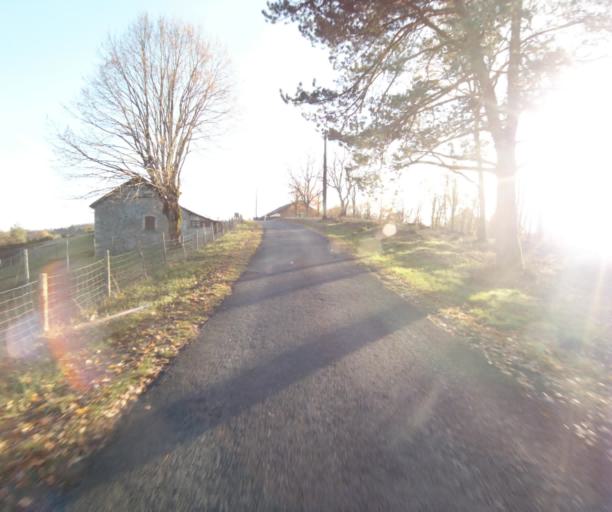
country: FR
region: Limousin
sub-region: Departement de la Correze
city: Laguenne
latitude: 45.2305
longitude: 1.8009
